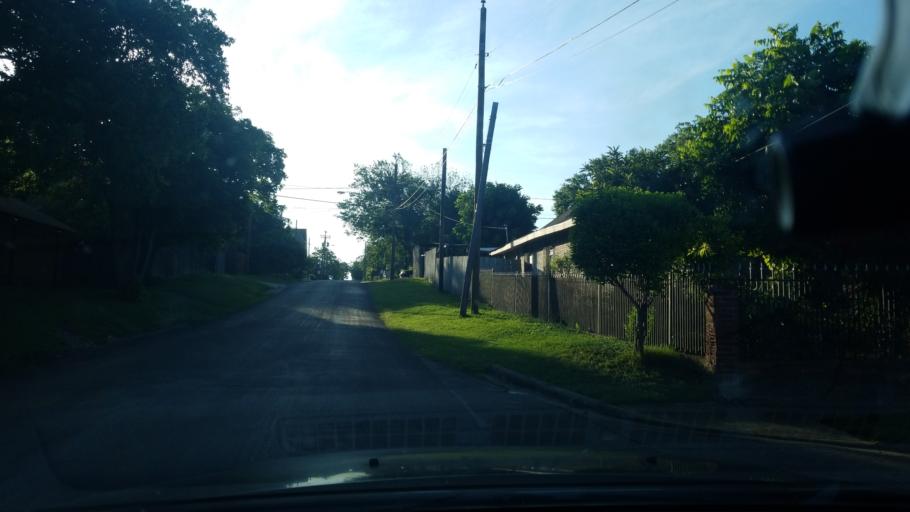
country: US
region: Texas
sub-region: Dallas County
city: Dallas
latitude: 32.7179
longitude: -96.8171
